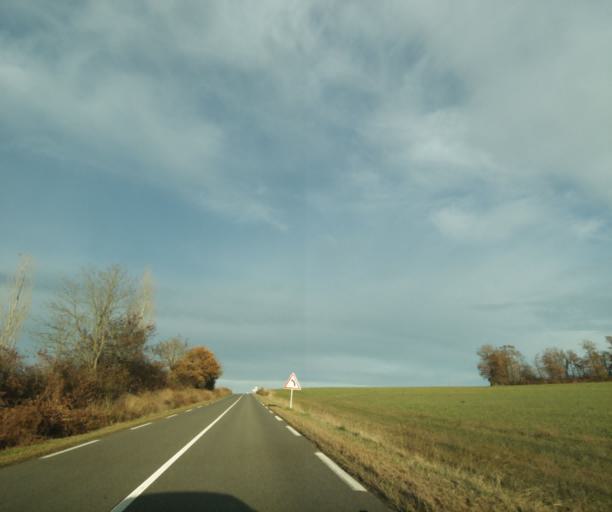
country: FR
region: Aquitaine
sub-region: Departement des Landes
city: Gabarret
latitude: 43.9677
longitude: 0.0031
